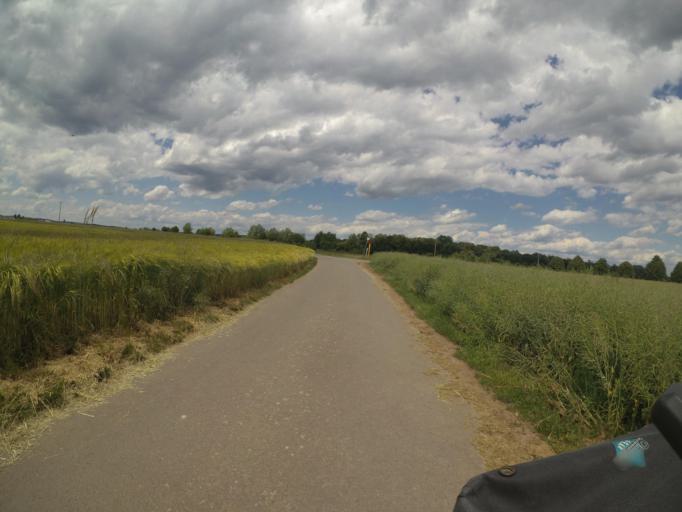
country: DE
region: Rheinland-Pfalz
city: Hauptstuhl
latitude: 49.4070
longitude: 7.4533
